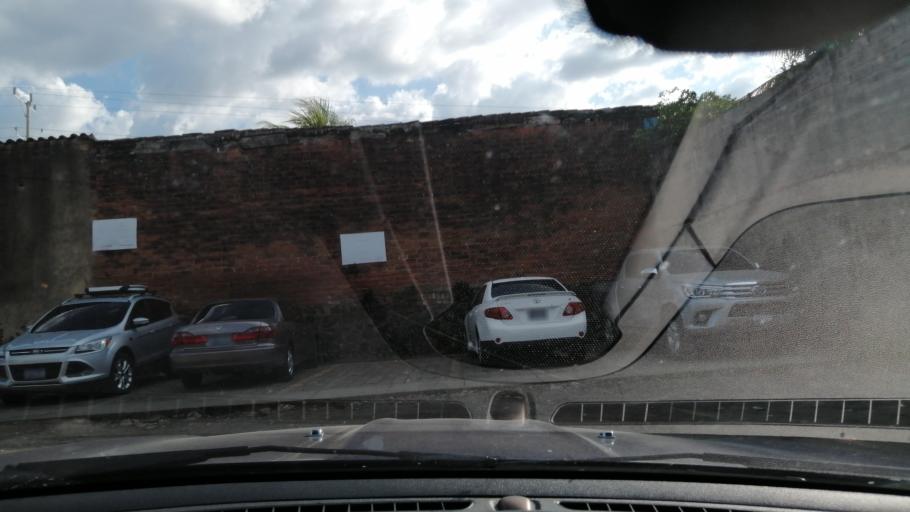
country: SV
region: Santa Ana
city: Santa Ana
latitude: 13.9834
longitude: -89.5618
